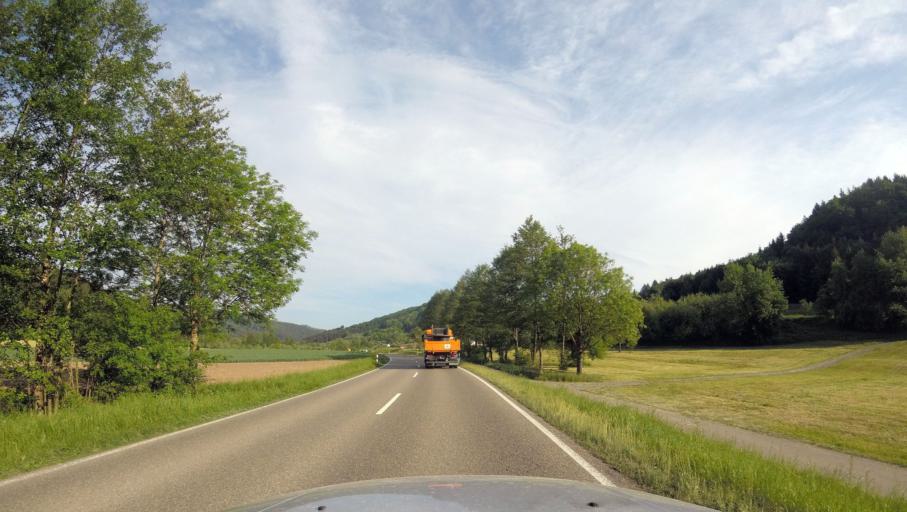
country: DE
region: Baden-Wuerttemberg
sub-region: Regierungsbezirk Stuttgart
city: Sulzbach an der Murr
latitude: 49.0147
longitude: 9.4725
